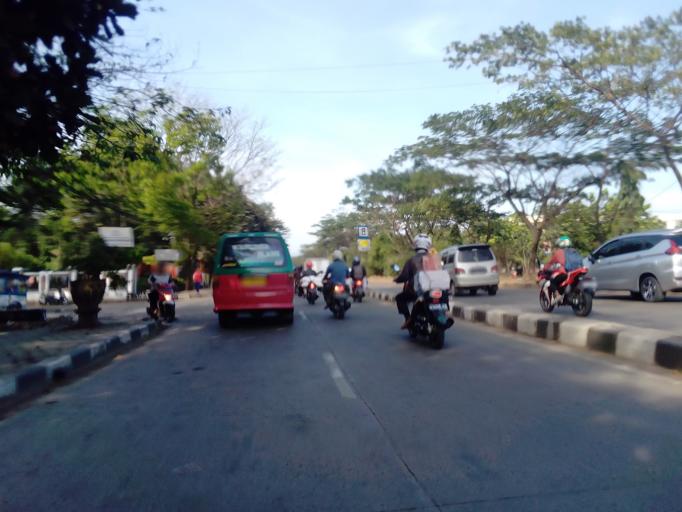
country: ID
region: West Java
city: Cileunyi
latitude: -6.9364
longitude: 107.6990
